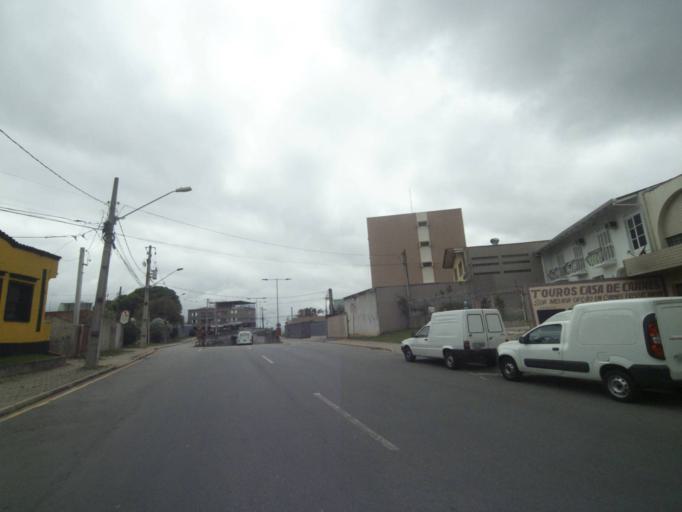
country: BR
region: Parana
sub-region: Curitiba
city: Curitiba
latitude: -25.4385
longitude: -49.2359
